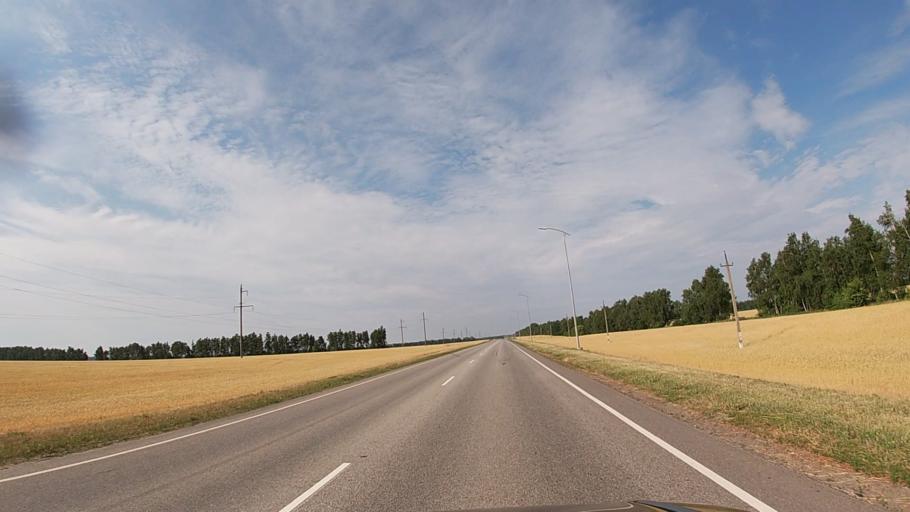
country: RU
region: Belgorod
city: Proletarskiy
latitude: 50.8239
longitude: 35.7591
